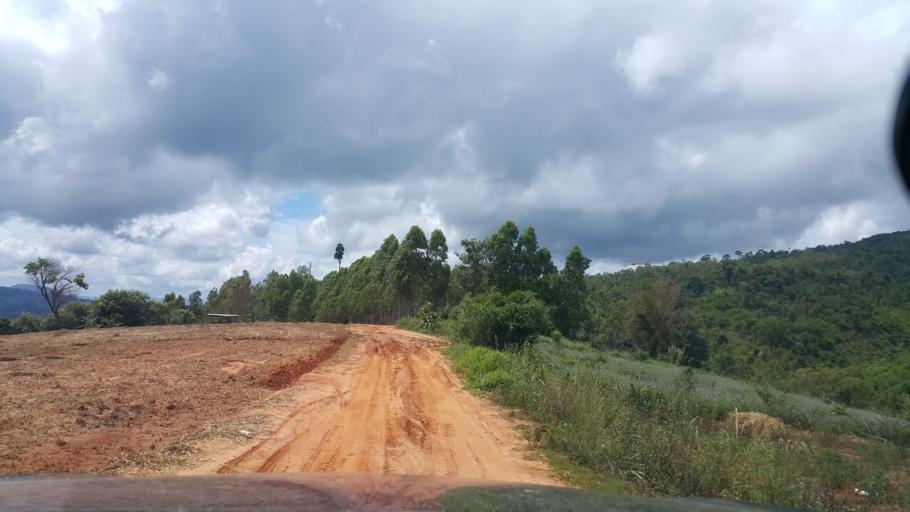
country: TH
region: Loei
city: Na Haeo
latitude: 17.5975
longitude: 100.9007
